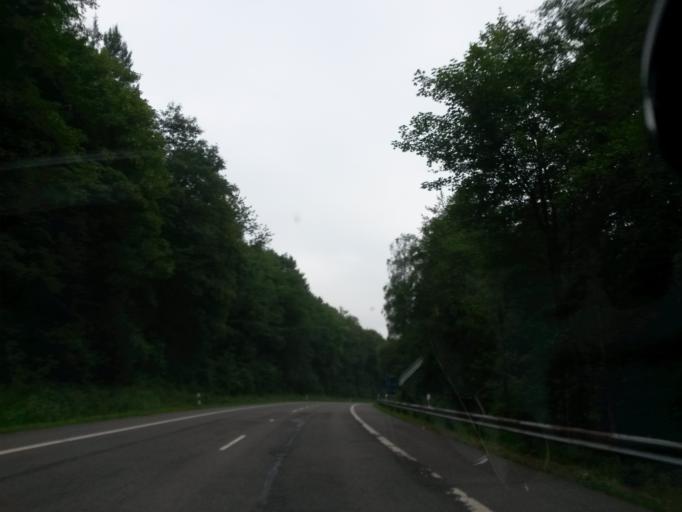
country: DE
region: North Rhine-Westphalia
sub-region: Regierungsbezirk Koln
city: Engelskirchen
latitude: 50.9785
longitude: 7.4342
